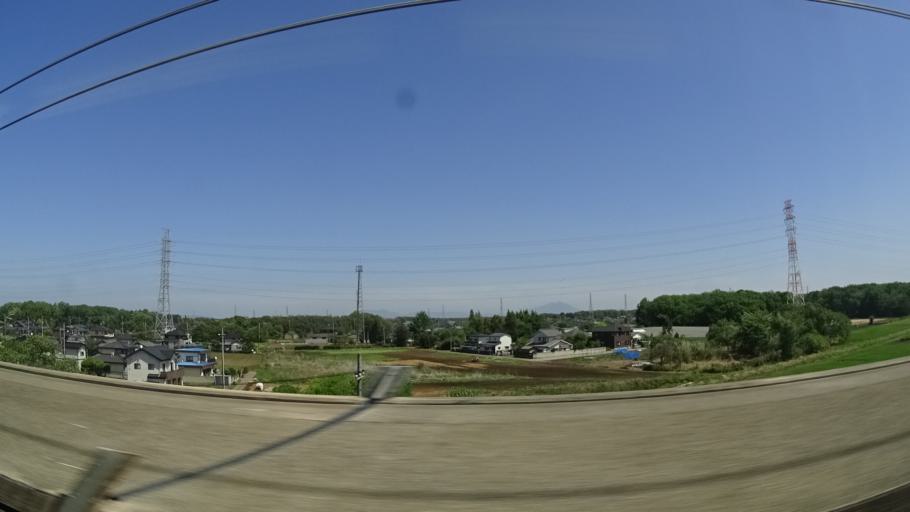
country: JP
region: Tochigi
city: Mibu
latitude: 36.3662
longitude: 139.8374
